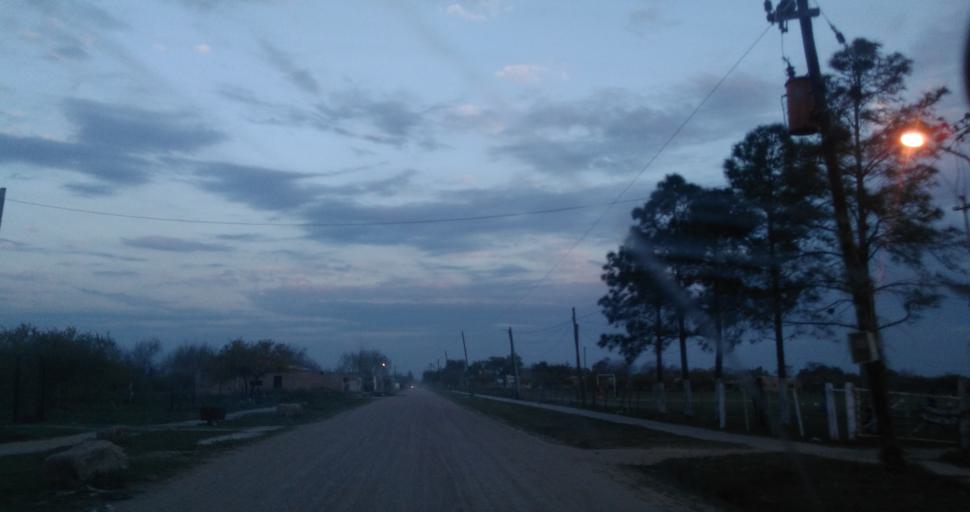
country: AR
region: Chaco
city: Resistencia
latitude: -27.4700
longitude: -59.0193
